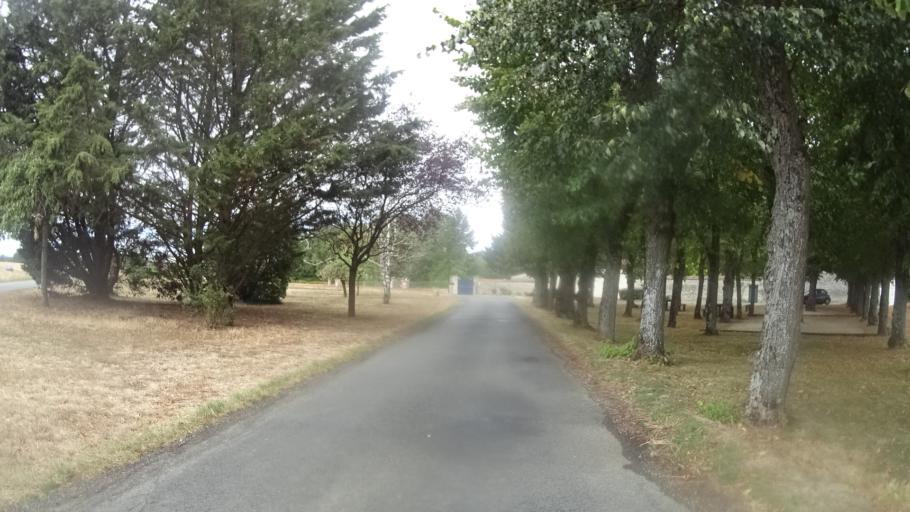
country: FR
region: Centre
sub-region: Departement du Loiret
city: Boynes
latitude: 48.1997
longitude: 2.4061
